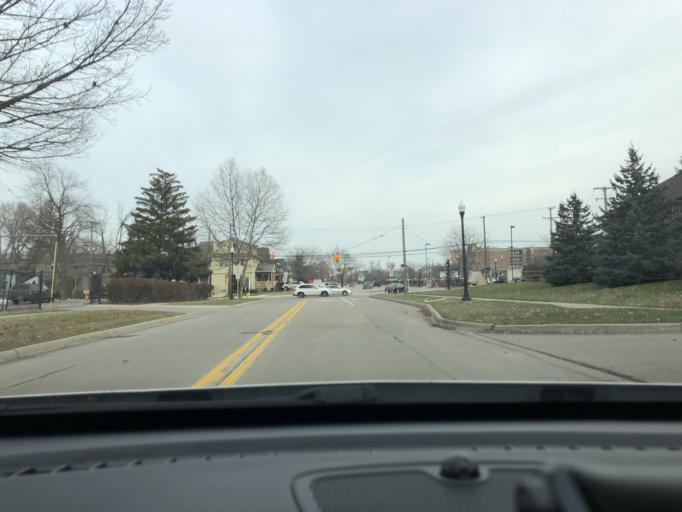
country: US
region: Michigan
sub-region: Wayne County
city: Dearborn Heights
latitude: 42.3056
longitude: -83.2525
